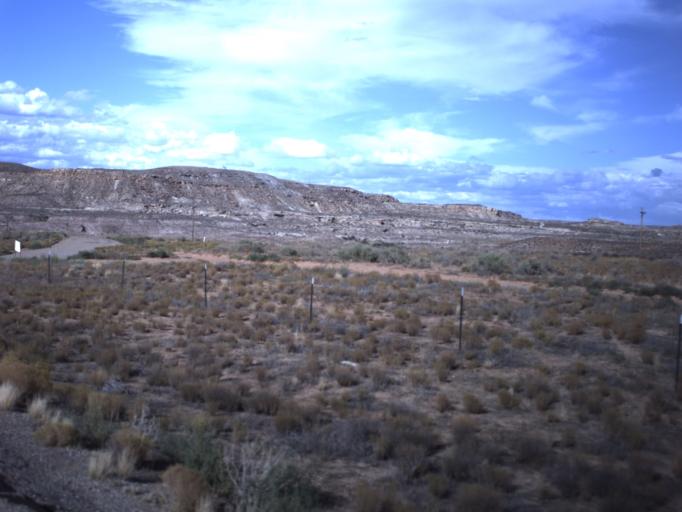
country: US
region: Utah
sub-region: San Juan County
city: Blanding
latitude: 37.3022
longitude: -109.2840
